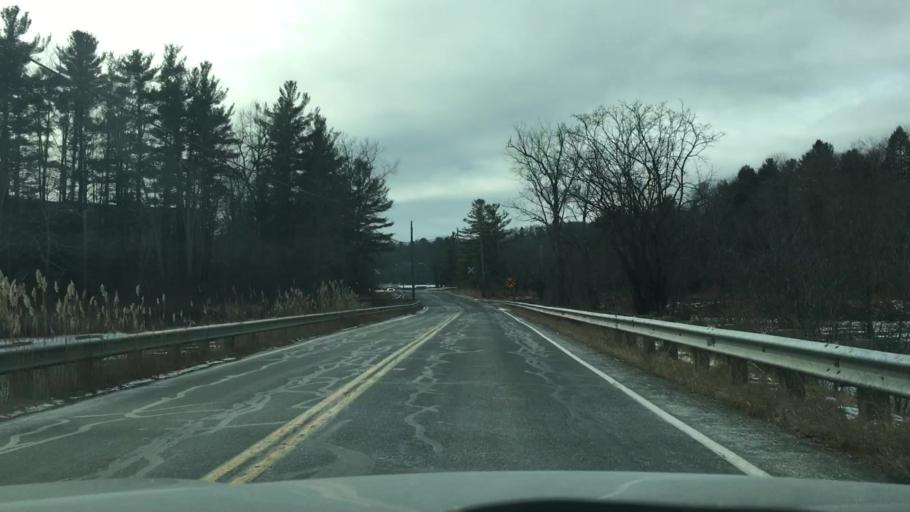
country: US
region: Massachusetts
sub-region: Berkshire County
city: Lee
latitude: 42.3204
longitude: -73.2416
